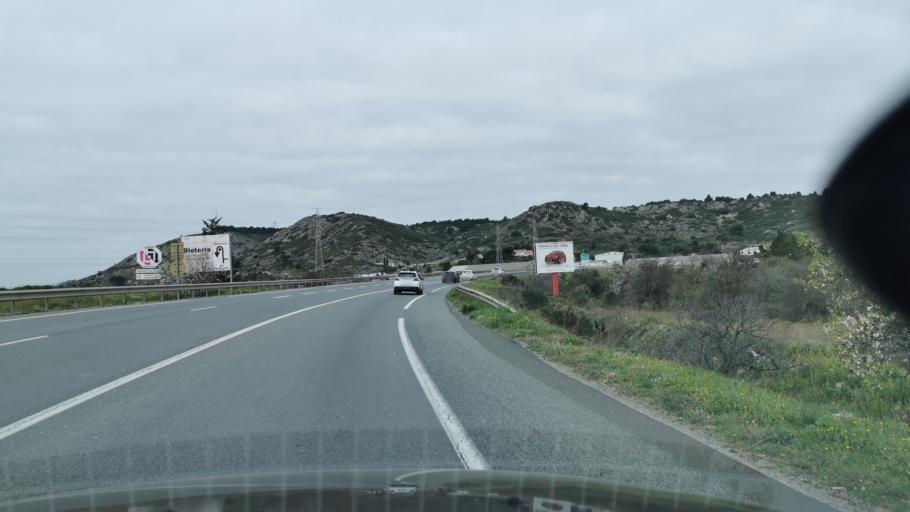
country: FR
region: Languedoc-Roussillon
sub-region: Departement de l'Aude
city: Narbonne
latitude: 43.1782
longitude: 2.9689
